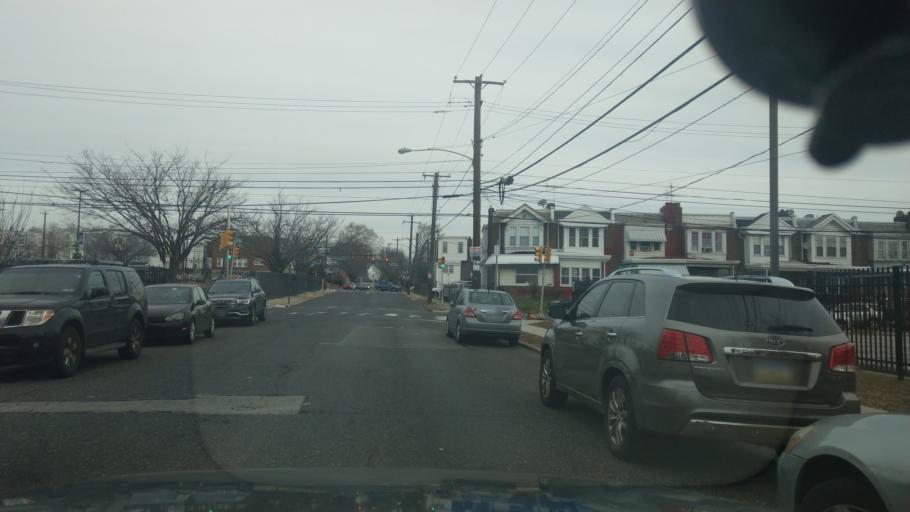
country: US
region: Pennsylvania
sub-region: Montgomery County
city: Wyncote
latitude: 40.0367
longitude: -75.1397
